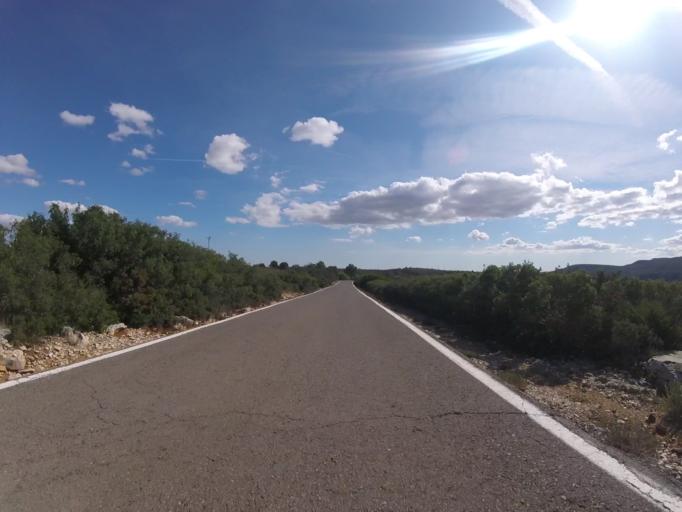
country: ES
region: Valencia
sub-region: Provincia de Castello
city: Albocasser
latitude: 40.3972
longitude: 0.0887
